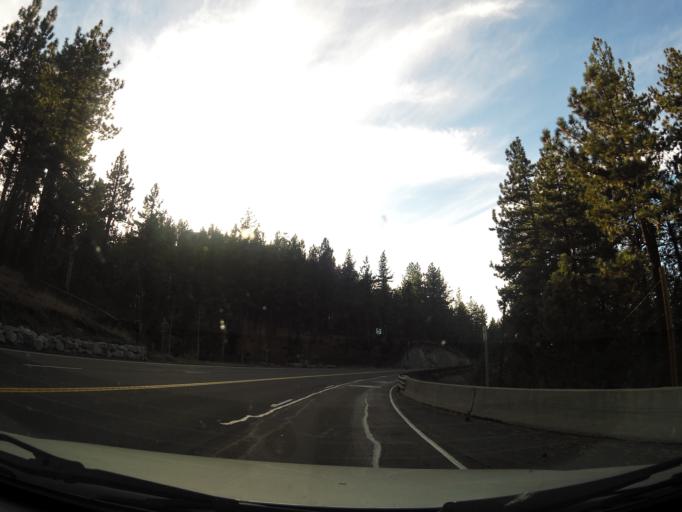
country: US
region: Nevada
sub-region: Douglas County
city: Kingsbury
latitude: 39.0026
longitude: -119.9490
